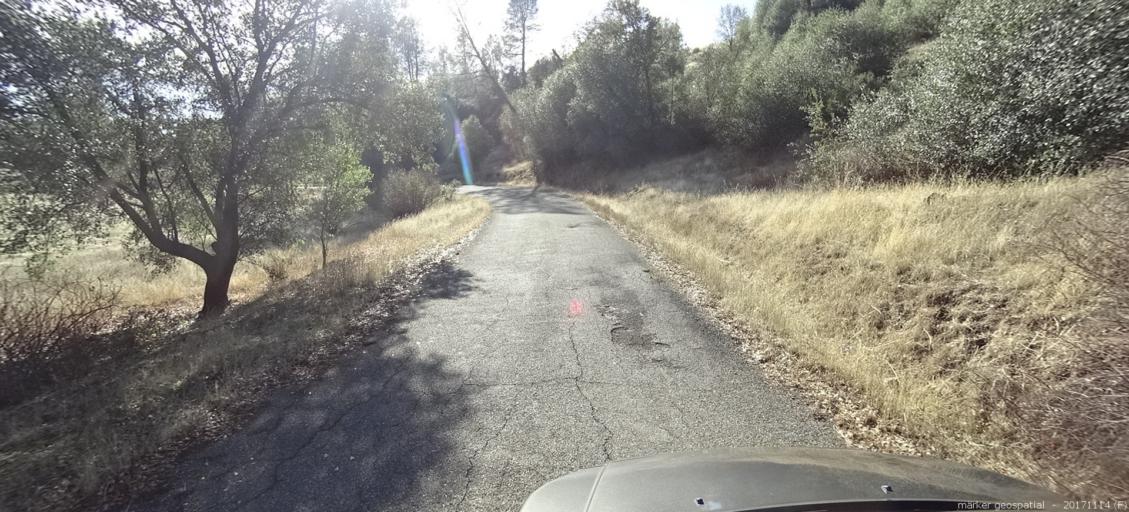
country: US
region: California
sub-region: Shasta County
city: Shasta
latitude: 40.3788
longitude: -122.5558
